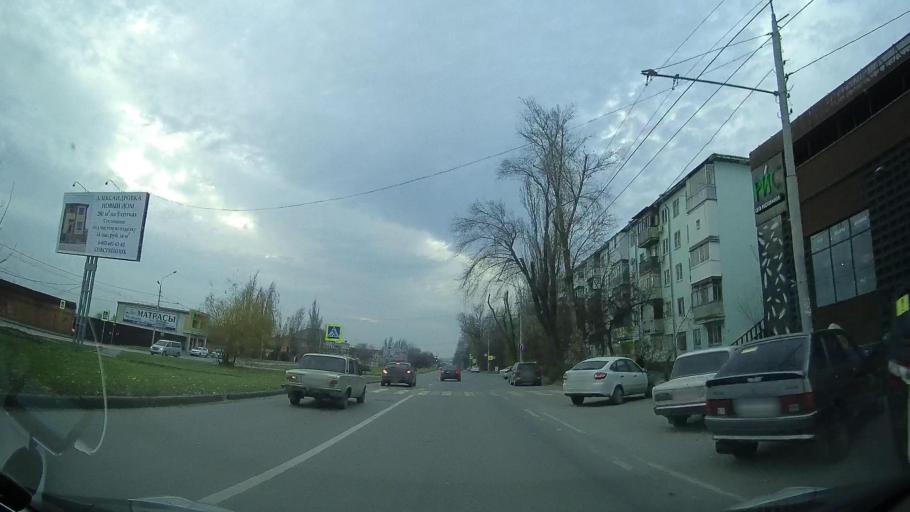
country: RU
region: Rostov
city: Aksay
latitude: 47.2374
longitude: 39.8177
